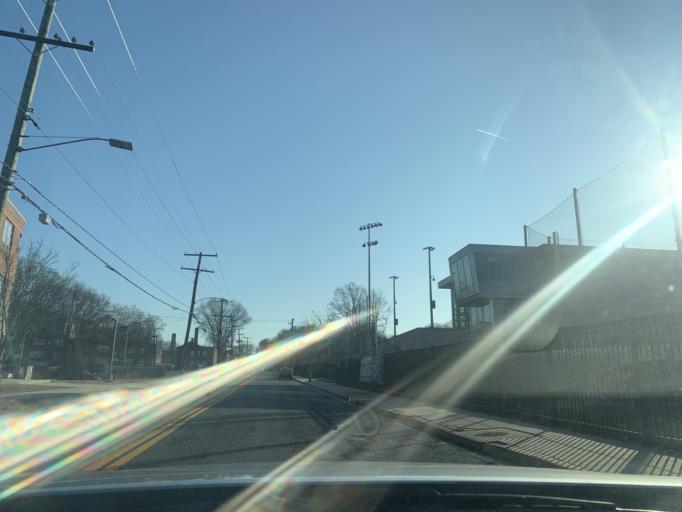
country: US
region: Maryland
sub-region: Prince George's County
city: Coral Hills
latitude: 38.8836
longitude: -76.9530
